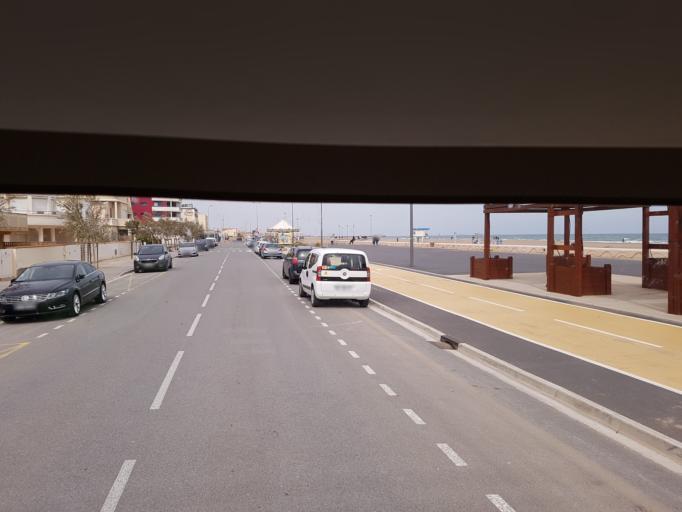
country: FR
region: Languedoc-Roussillon
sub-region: Departement de l'Aude
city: Armissan
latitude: 43.1576
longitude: 3.1663
